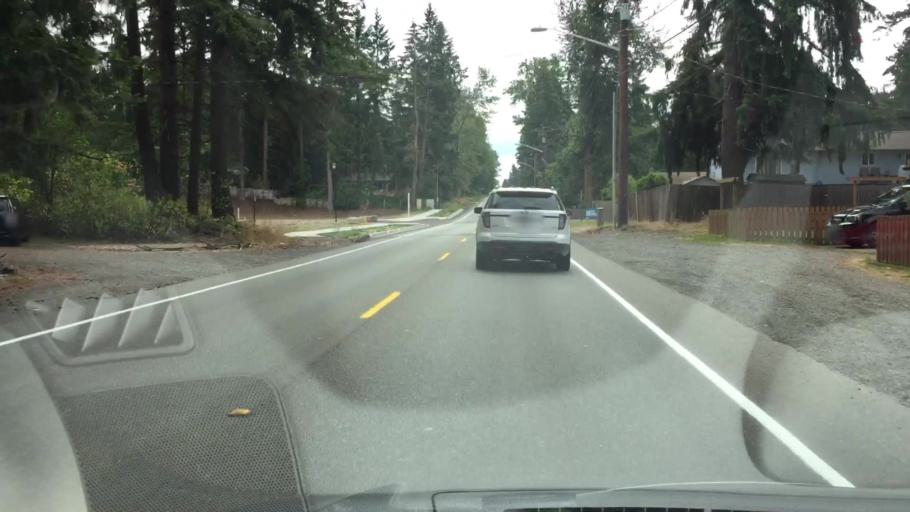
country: US
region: Washington
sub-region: Pierce County
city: South Hill
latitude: 47.1241
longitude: -122.2666
